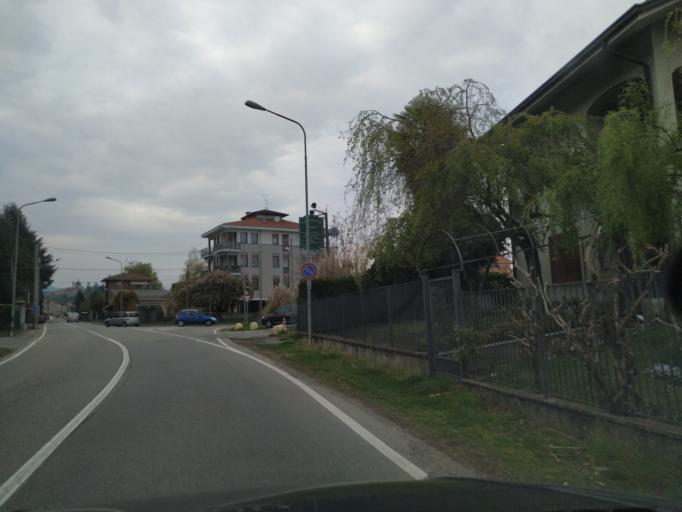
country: IT
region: Piedmont
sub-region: Provincia di Novara
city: Borgomanero
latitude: 45.6946
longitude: 8.4538
